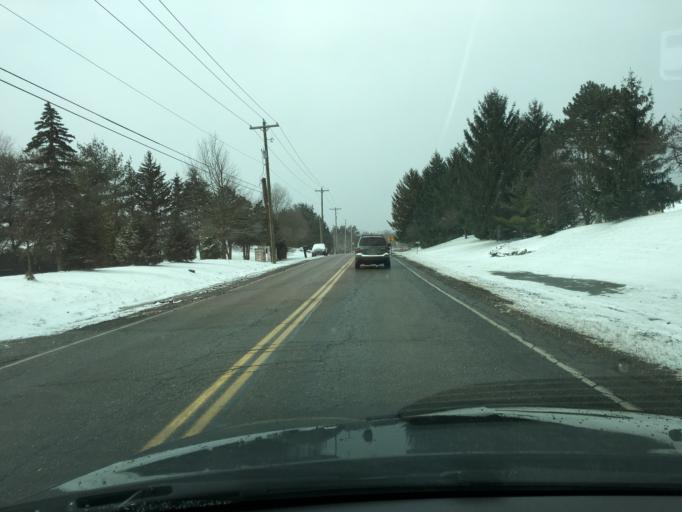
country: US
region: Ohio
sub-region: Summit County
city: Fairlawn
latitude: 41.1404
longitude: -81.5845
